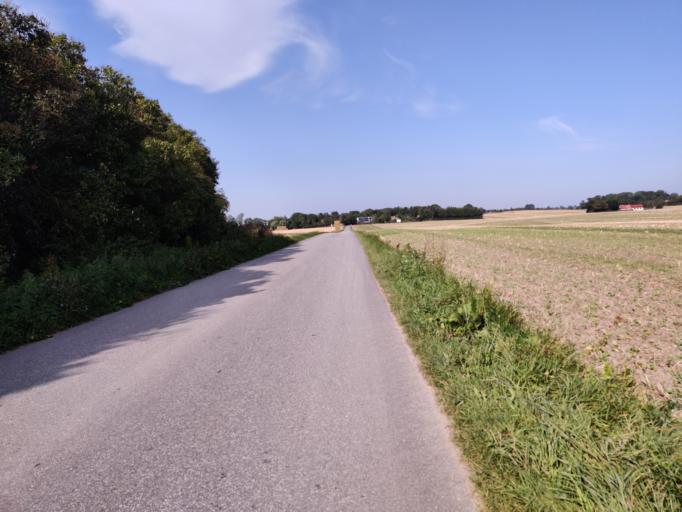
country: DK
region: Zealand
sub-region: Guldborgsund Kommune
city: Nykobing Falster
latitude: 54.6930
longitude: 11.9026
